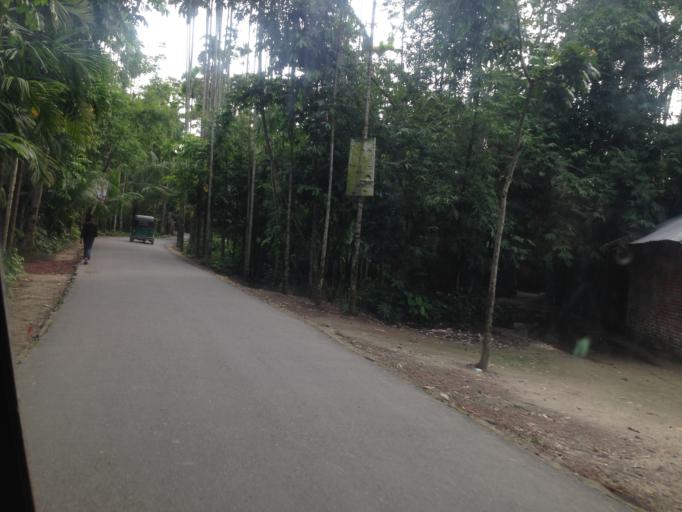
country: BD
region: Chittagong
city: Raipur
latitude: 23.0297
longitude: 90.7072
